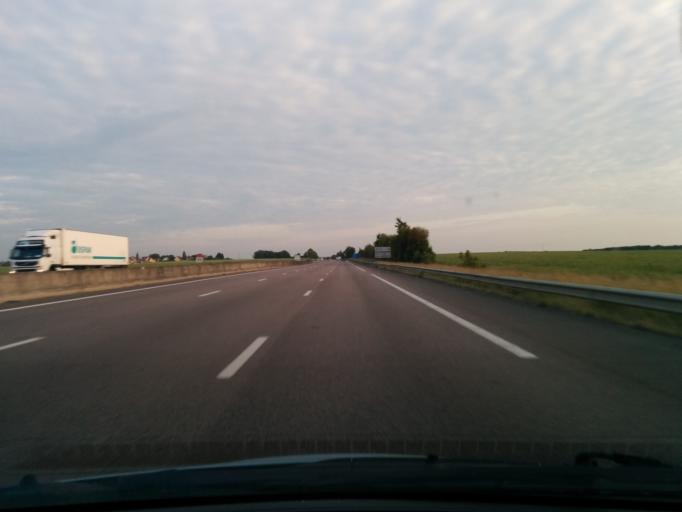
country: FR
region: Haute-Normandie
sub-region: Departement de l'Eure
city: La Chapelle-Reanville
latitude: 49.0679
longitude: 1.4138
